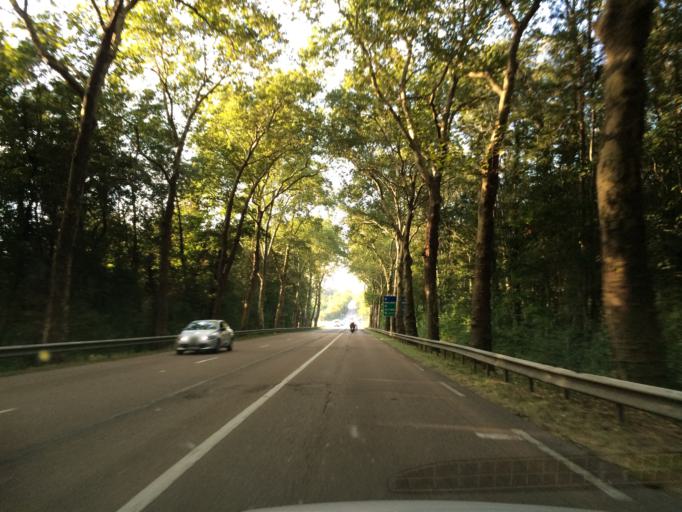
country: FR
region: Bourgogne
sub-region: Departement de l'Yonne
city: Moneteau
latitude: 47.8326
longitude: 3.5532
